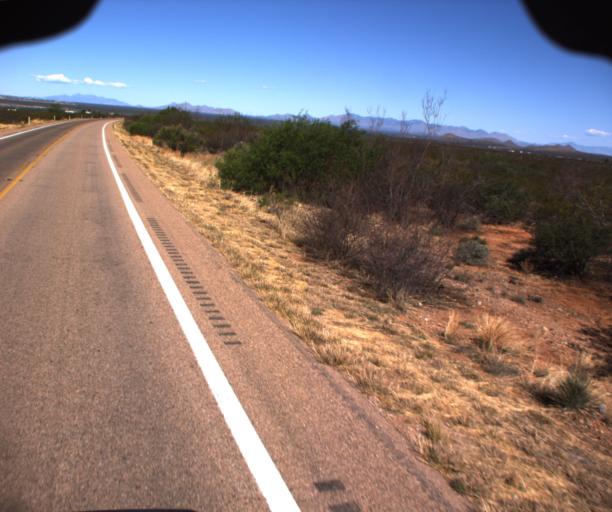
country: US
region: Arizona
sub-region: Cochise County
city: Sierra Vista Southeast
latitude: 31.5445
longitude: -110.0918
